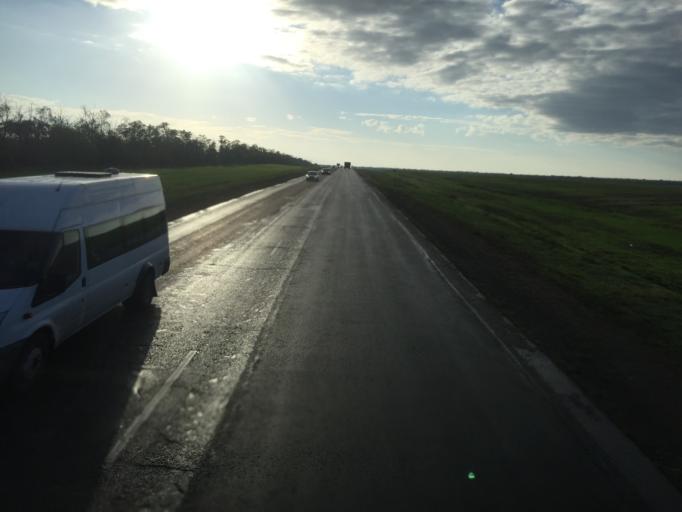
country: RU
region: Rostov
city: Kagal'nitskaya
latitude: 46.8648
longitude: 40.1782
